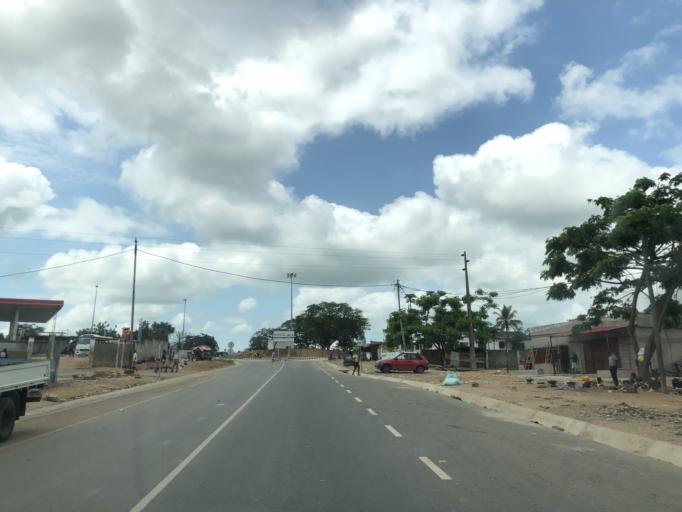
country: AO
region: Cuanza Norte
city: N'dalatando
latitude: -9.6803
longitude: 14.4731
